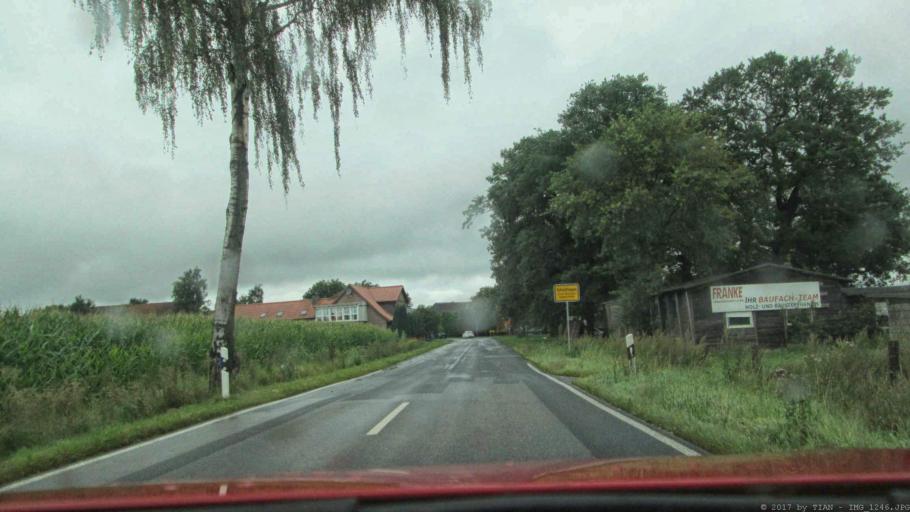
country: DE
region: Lower Saxony
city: Wittingen
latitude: 52.6526
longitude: 10.8054
